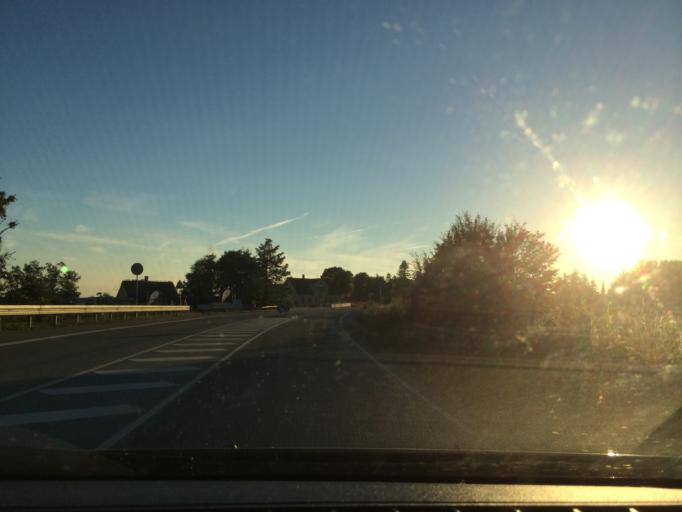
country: DK
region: Zealand
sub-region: Vordingborg Kommune
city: Stege
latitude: 54.9666
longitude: 12.2073
